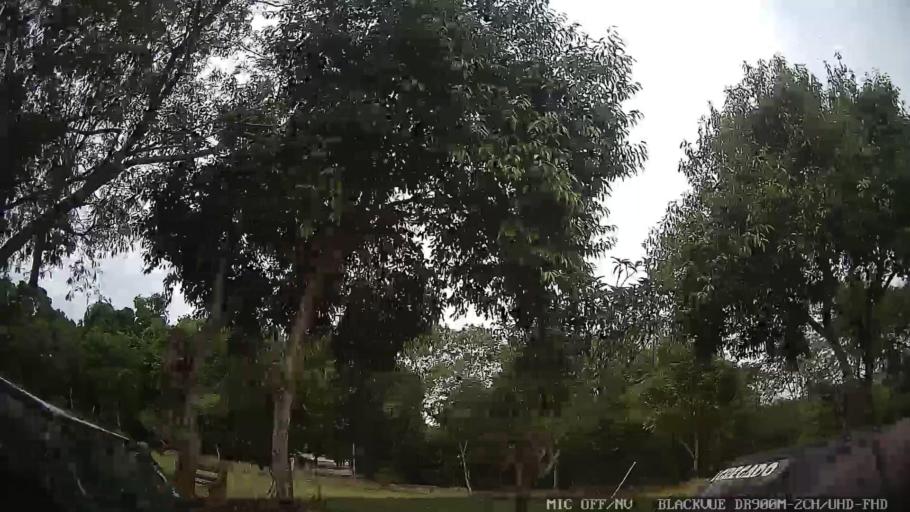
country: BR
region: Sao Paulo
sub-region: Salto
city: Salto
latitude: -23.2172
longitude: -47.2809
